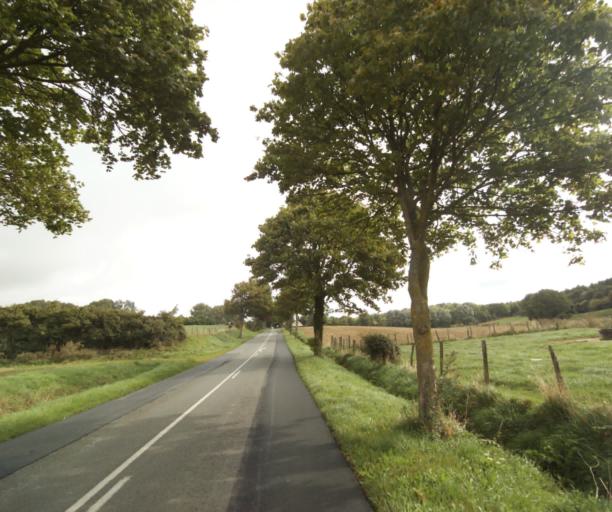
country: FR
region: Nord-Pas-de-Calais
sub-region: Departement du Pas-de-Calais
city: Etaples
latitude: 50.5221
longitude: 1.6740
